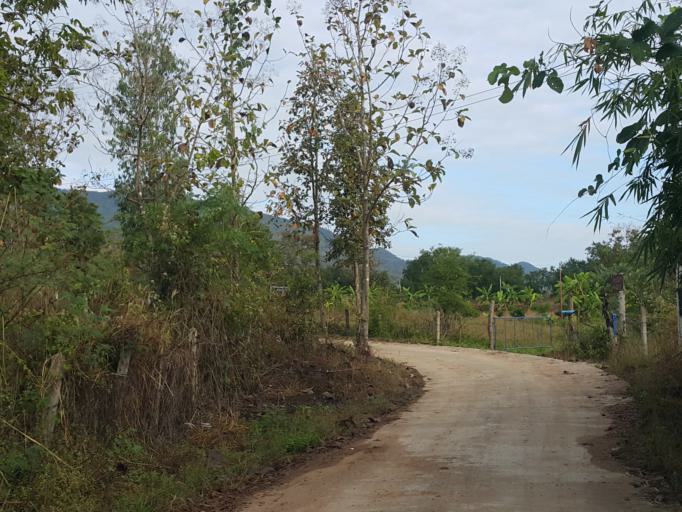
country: TH
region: Lampang
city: Mae Mo
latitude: 18.2537
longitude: 99.6019
